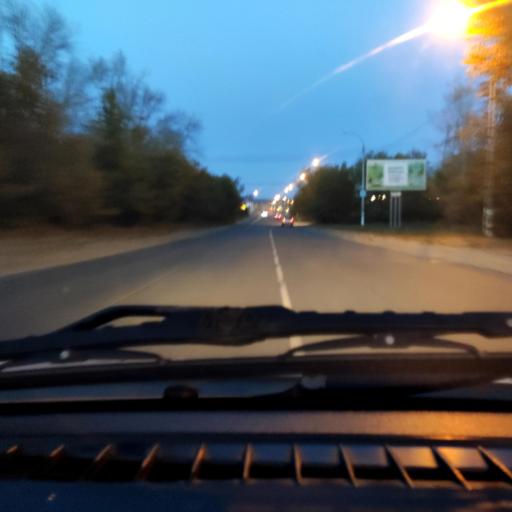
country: RU
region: Samara
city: Zhigulevsk
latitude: 53.4814
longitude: 49.5013
